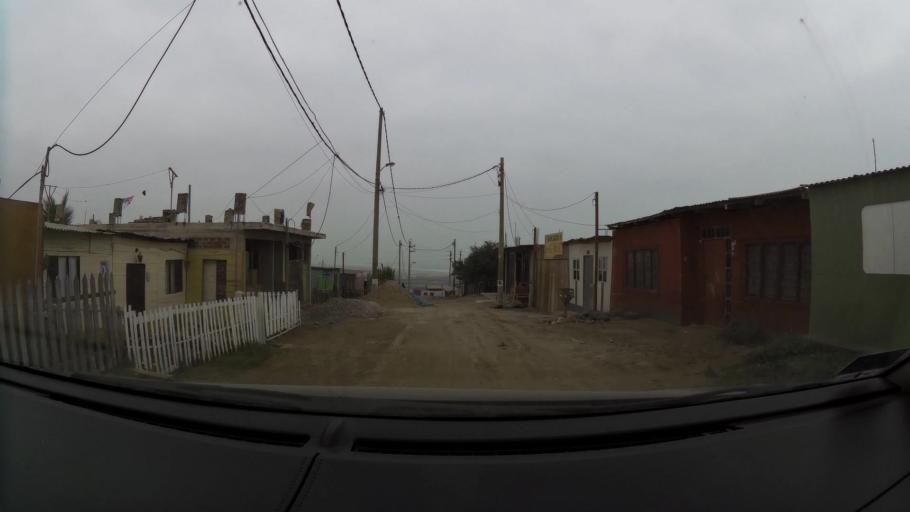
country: PE
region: Lima
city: Ventanilla
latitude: -11.8511
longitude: -77.1479
